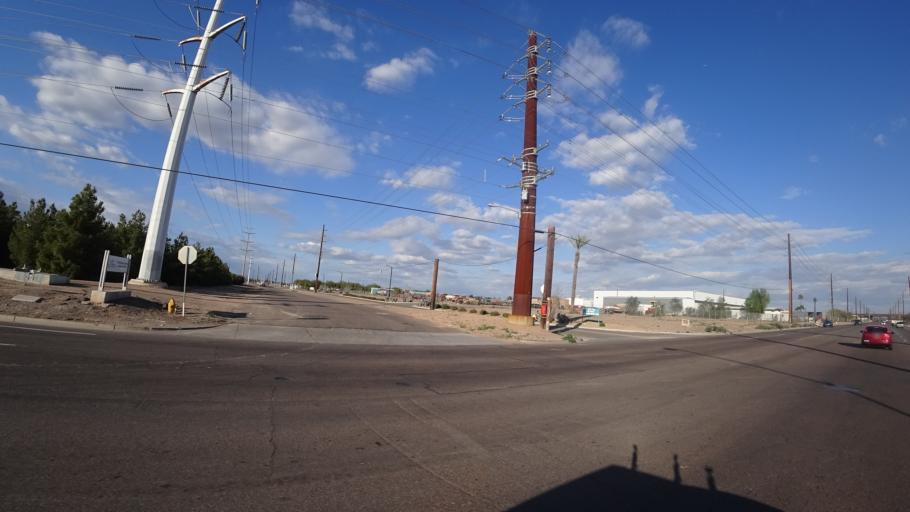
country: US
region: Arizona
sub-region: Maricopa County
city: Glendale
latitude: 33.5525
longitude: -112.2119
